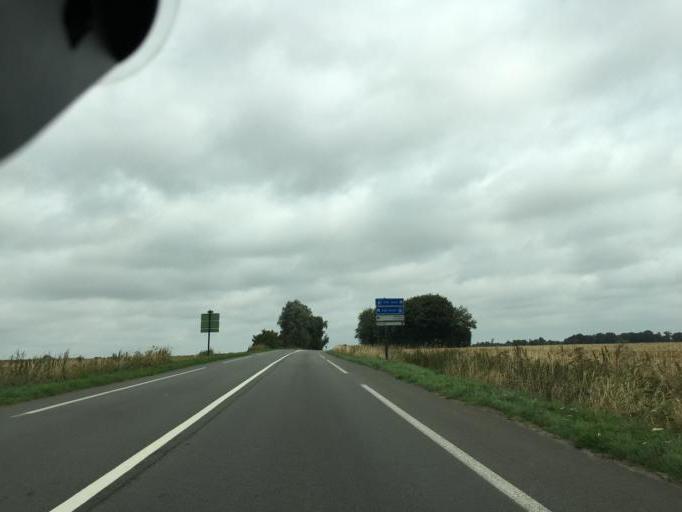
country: FR
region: Nord-Pas-de-Calais
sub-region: Departement du Pas-de-Calais
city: Saint-Pol-sur-Ternoise
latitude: 50.4036
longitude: 2.3627
